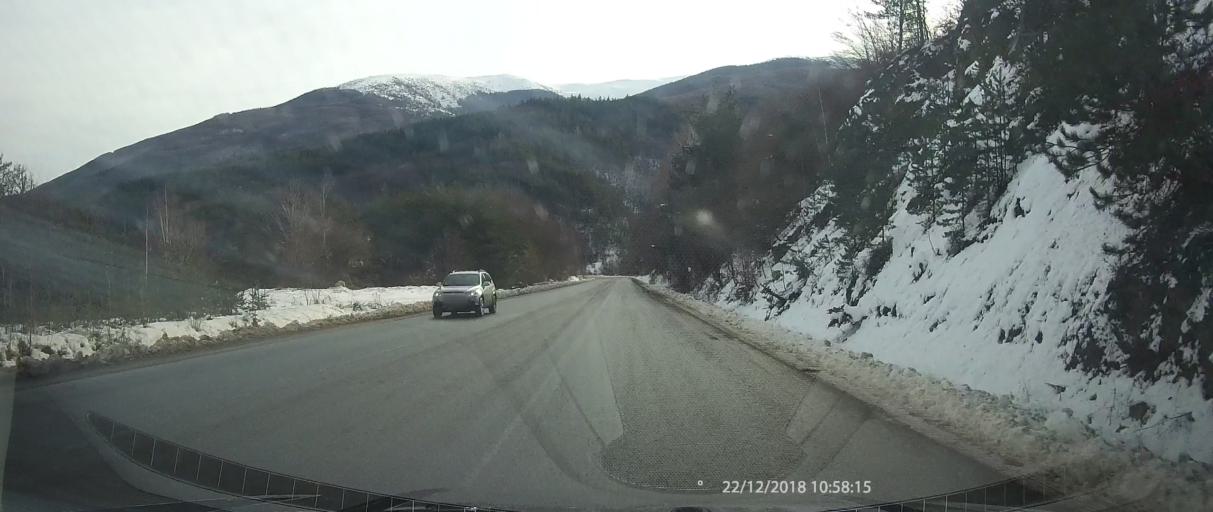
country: MK
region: Kriva Palanka
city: Kriva Palanka
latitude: 42.2182
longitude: 22.4672
